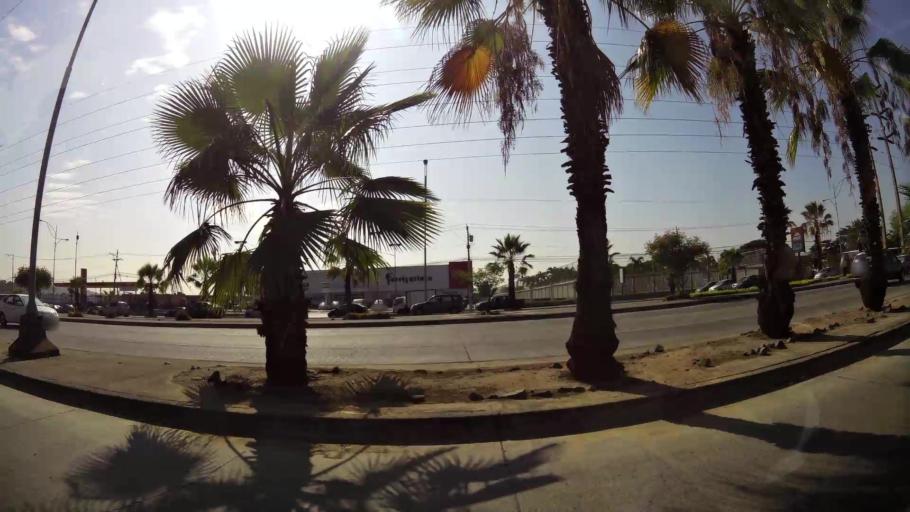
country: EC
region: Guayas
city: Eloy Alfaro
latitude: -2.0935
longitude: -79.9126
